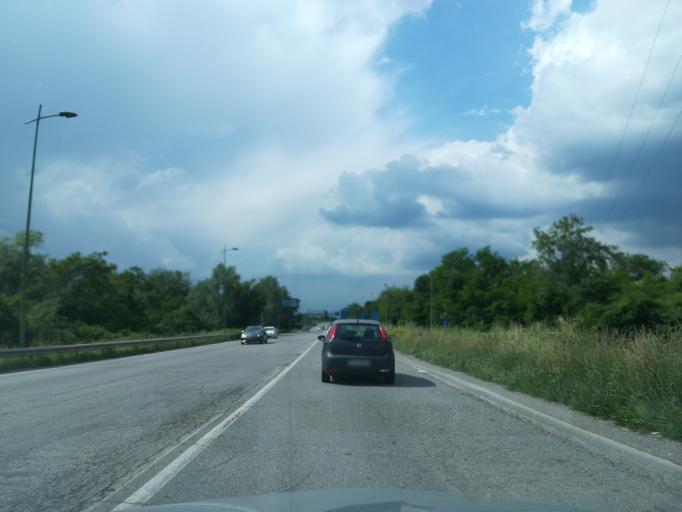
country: IT
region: Lombardy
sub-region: Provincia di Bergamo
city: Grassobbio
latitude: 45.6532
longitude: 9.7395
